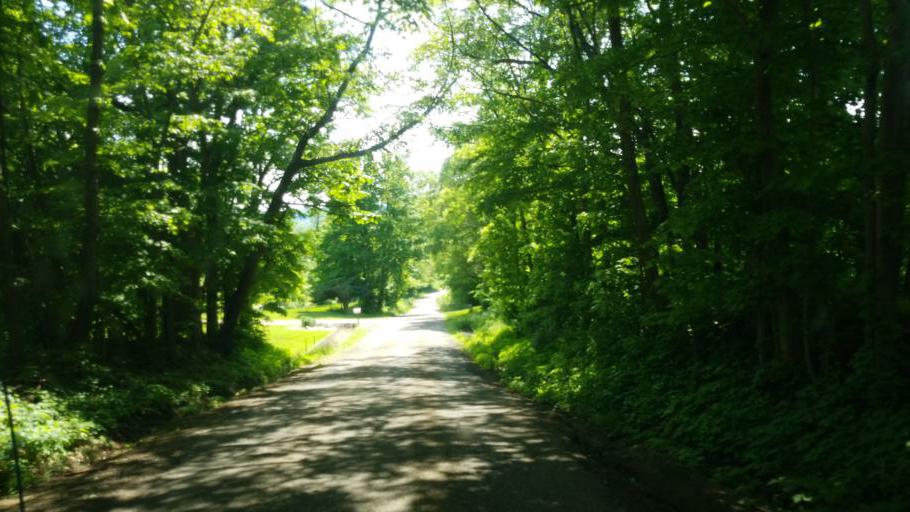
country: US
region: Ohio
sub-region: Sandusky County
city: Bellville
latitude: 40.6601
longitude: -82.5350
